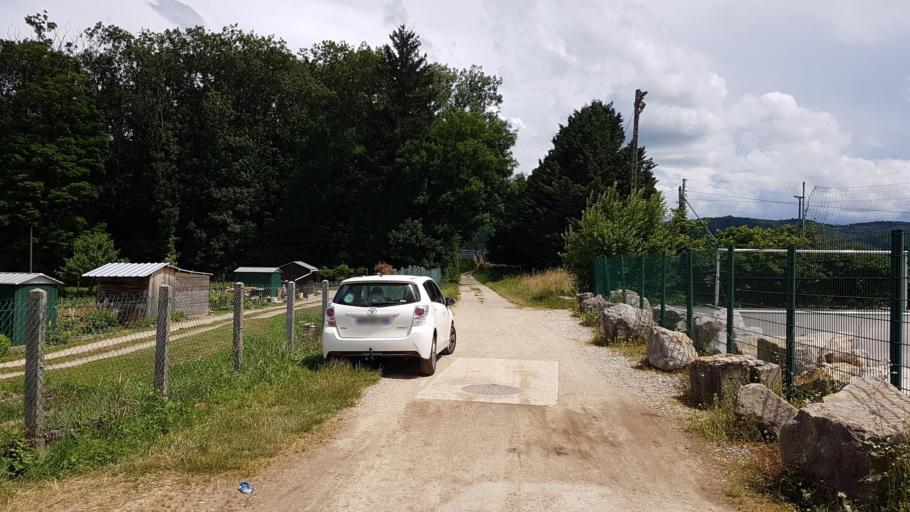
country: FR
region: Franche-Comte
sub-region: Departement du Jura
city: Perrigny
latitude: 46.6669
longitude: 5.5738
